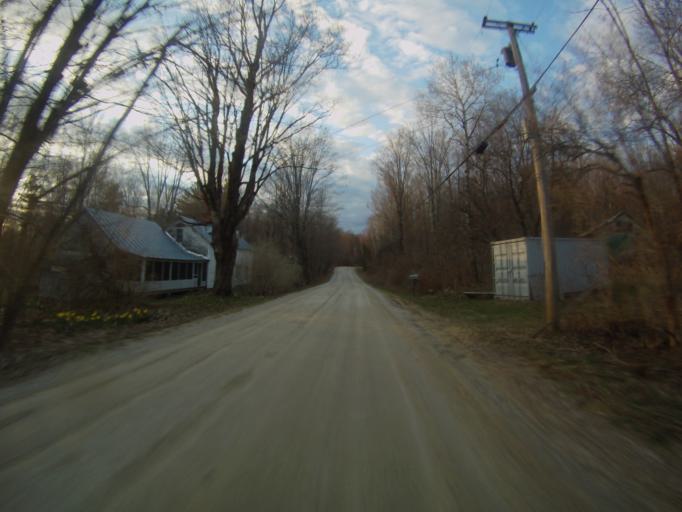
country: US
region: Vermont
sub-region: Rutland County
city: Brandon
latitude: 43.8531
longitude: -72.9986
